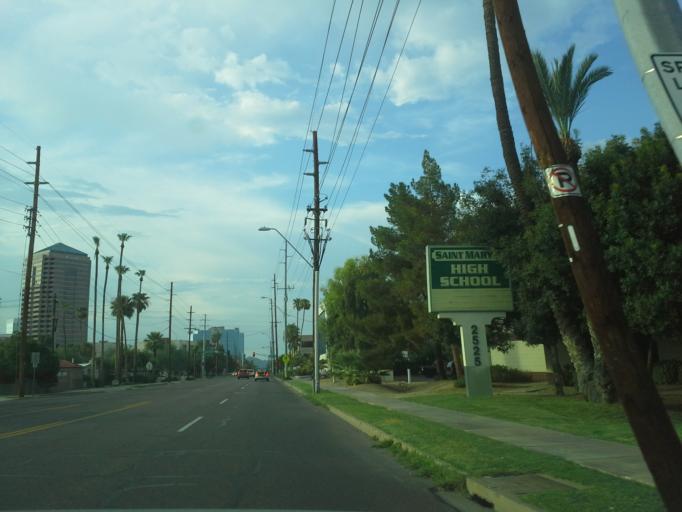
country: US
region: Arizona
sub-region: Maricopa County
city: Phoenix
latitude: 33.4748
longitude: -112.0694
